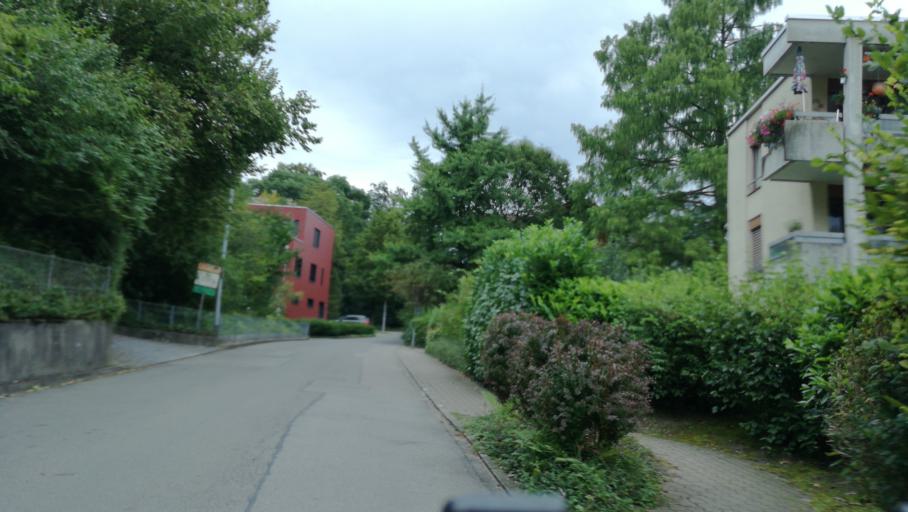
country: CH
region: Lucerne
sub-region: Lucerne-Stadt District
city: Luzern
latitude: 47.0688
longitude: 8.3167
